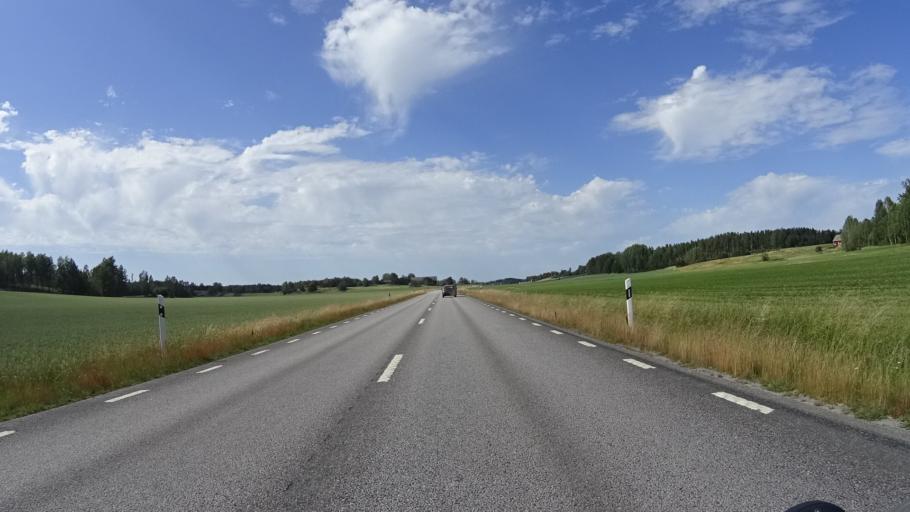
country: SE
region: OEstergoetland
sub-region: Linkopings Kommun
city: Sturefors
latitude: 58.3326
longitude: 15.8528
